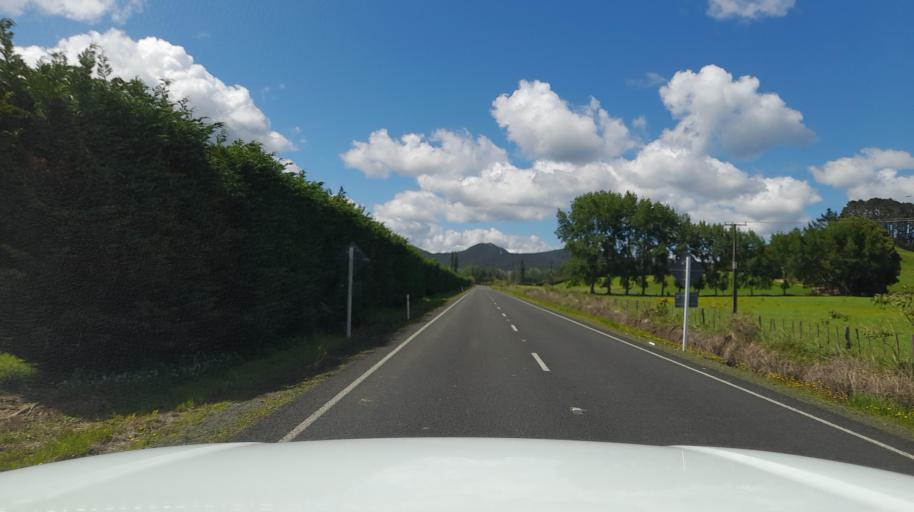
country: NZ
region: Northland
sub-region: Far North District
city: Taipa
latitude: -35.0715
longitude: 173.5051
